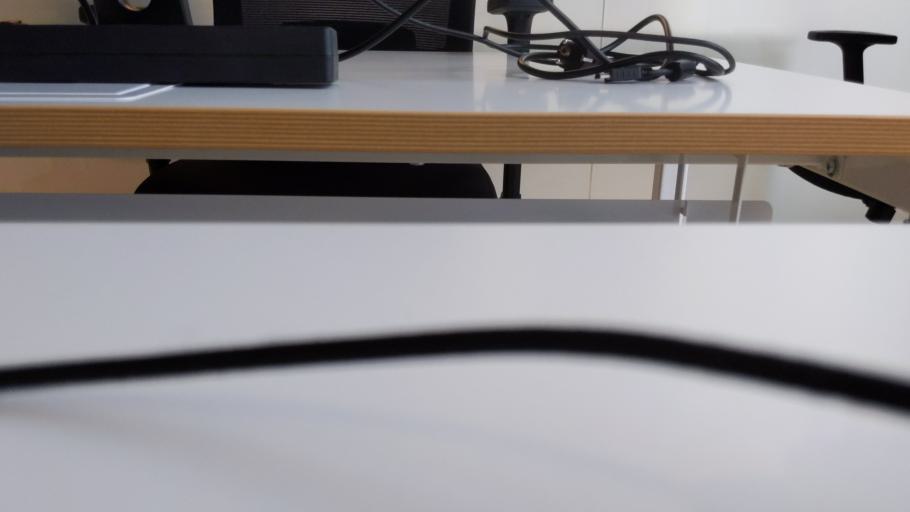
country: RU
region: Moskovskaya
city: Shevlyakovo
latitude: 56.3890
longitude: 36.8622
